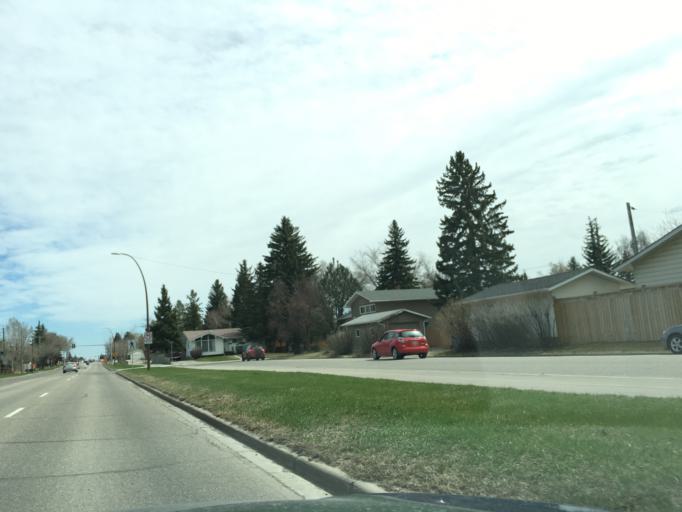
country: CA
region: Alberta
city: Calgary
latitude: 50.9796
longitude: -114.0909
